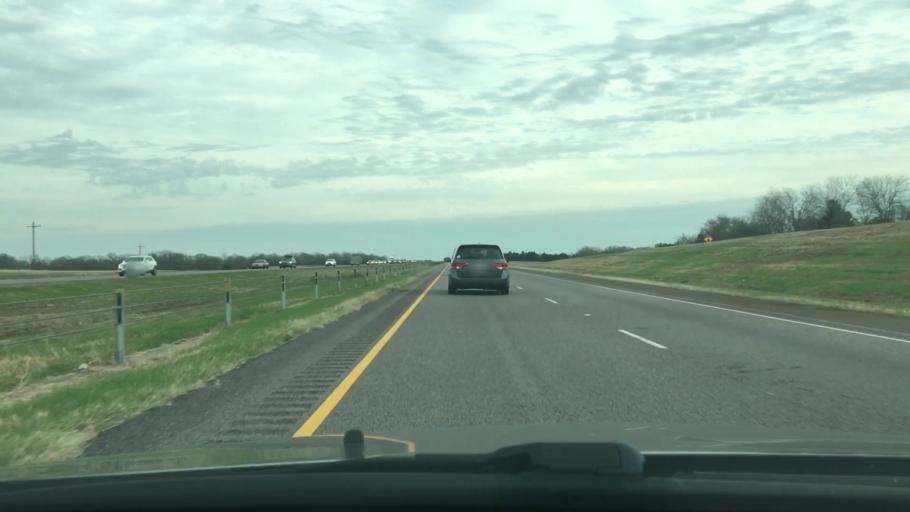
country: US
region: Texas
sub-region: Madison County
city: Madisonville
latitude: 30.9500
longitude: -95.8608
